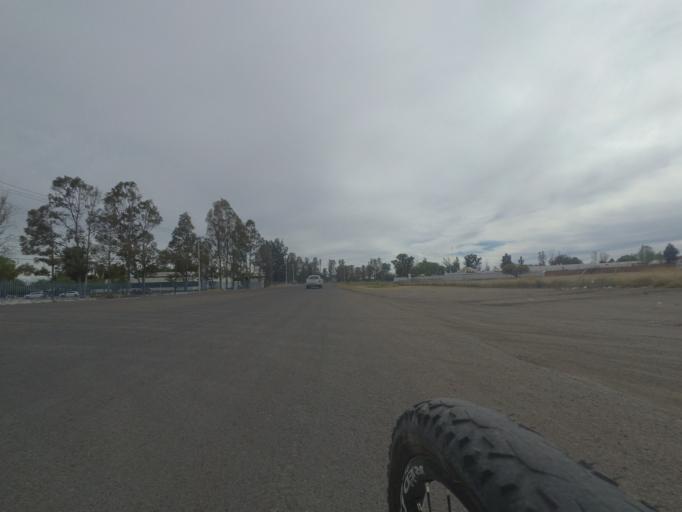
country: MX
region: Aguascalientes
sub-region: Aguascalientes
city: La Loma de los Negritos
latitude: 21.8408
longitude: -102.3546
